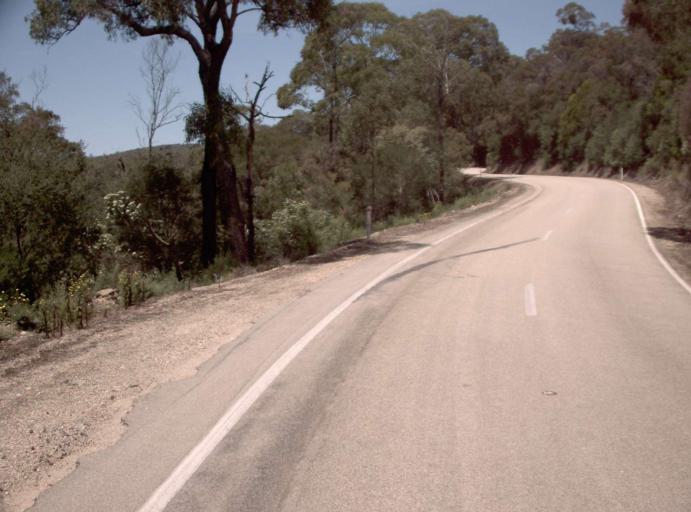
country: AU
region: Victoria
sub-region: East Gippsland
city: Lakes Entrance
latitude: -37.5606
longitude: 147.8867
